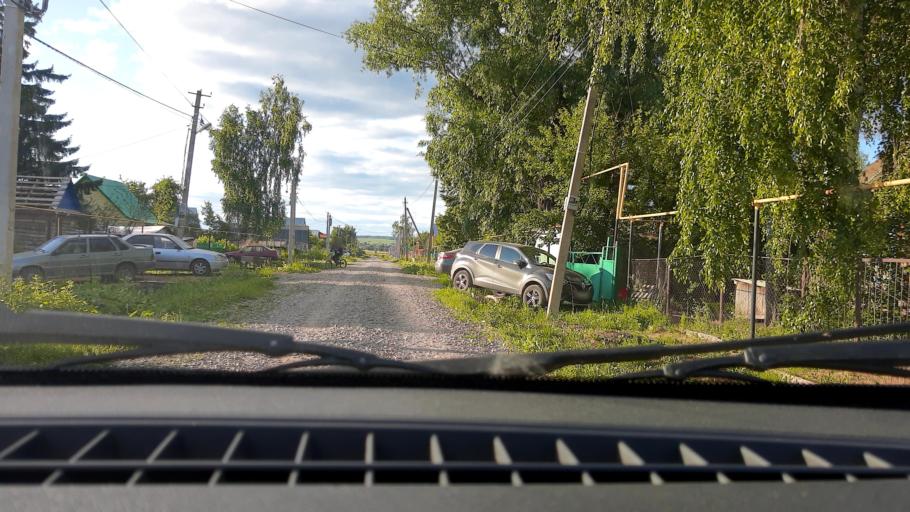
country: RU
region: Bashkortostan
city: Mikhaylovka
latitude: 54.8822
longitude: 55.8776
